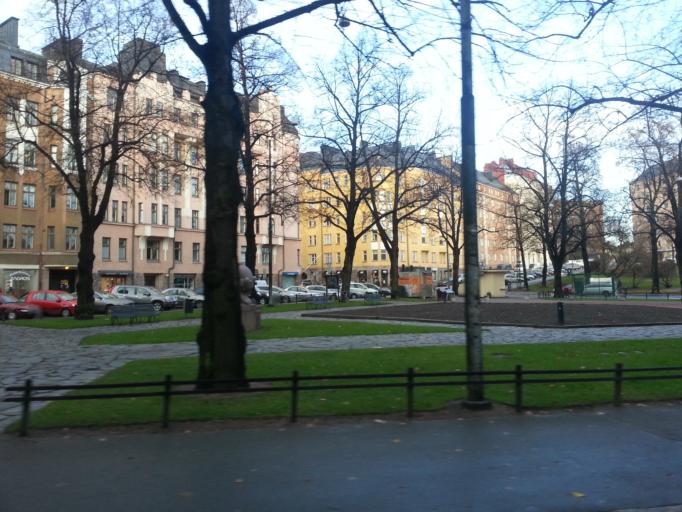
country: FI
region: Uusimaa
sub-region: Helsinki
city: Helsinki
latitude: 60.1839
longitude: 24.9518
